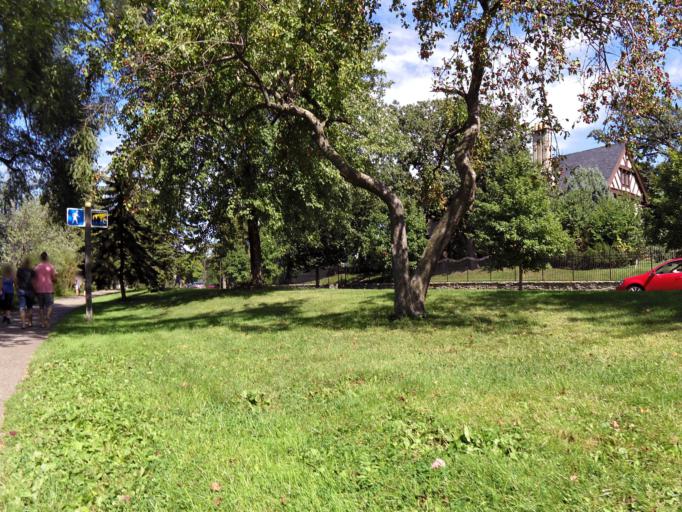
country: US
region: Minnesota
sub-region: Hennepin County
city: Saint Louis Park
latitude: 44.9570
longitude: -93.3039
